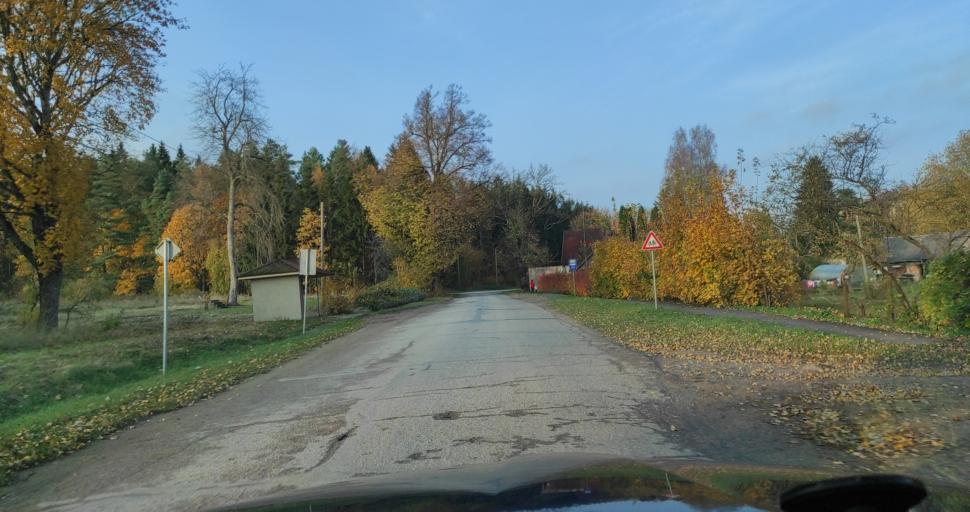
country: LV
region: Vainode
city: Vainode
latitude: 56.4336
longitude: 21.8725
